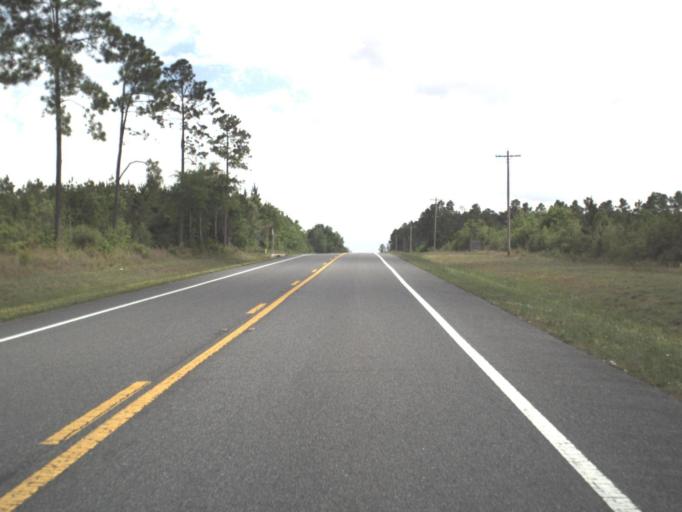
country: US
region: Florida
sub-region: Santa Rosa County
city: Wallace
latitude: 30.8322
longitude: -87.1401
